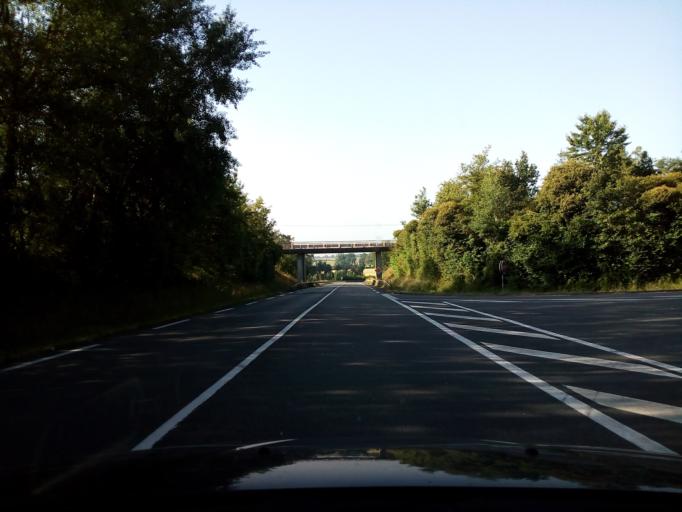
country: FR
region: Poitou-Charentes
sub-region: Departement de la Charente
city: Confolens
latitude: 46.0520
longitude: 0.6670
